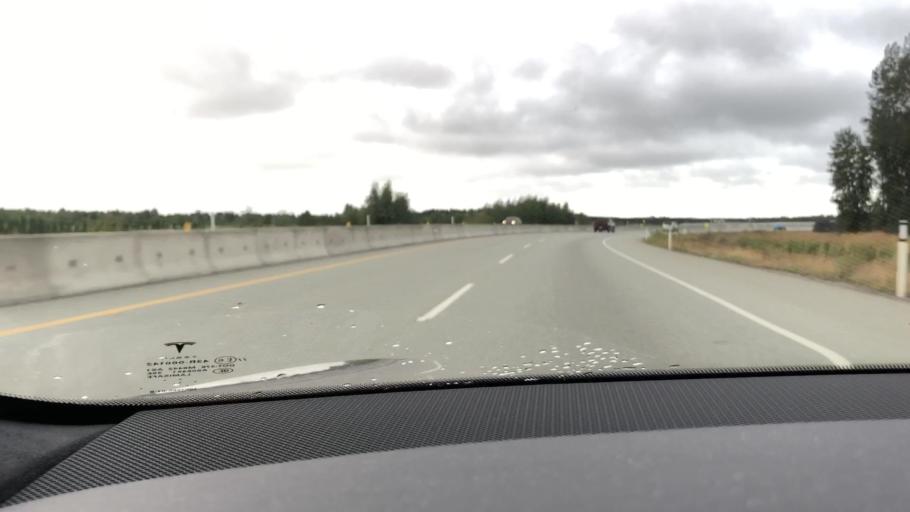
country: CA
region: British Columbia
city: Ladner
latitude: 49.1308
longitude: -123.0130
